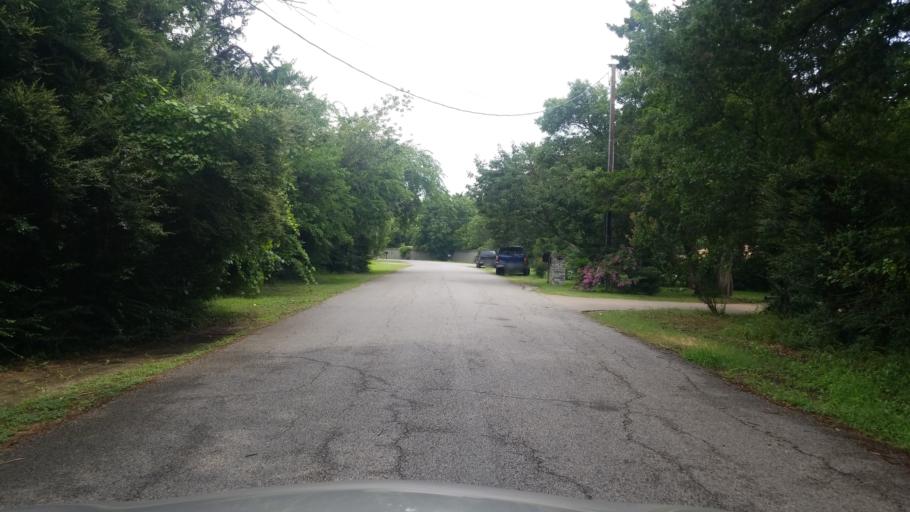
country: US
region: Texas
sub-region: Dallas County
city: Duncanville
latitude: 32.6791
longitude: -96.9295
